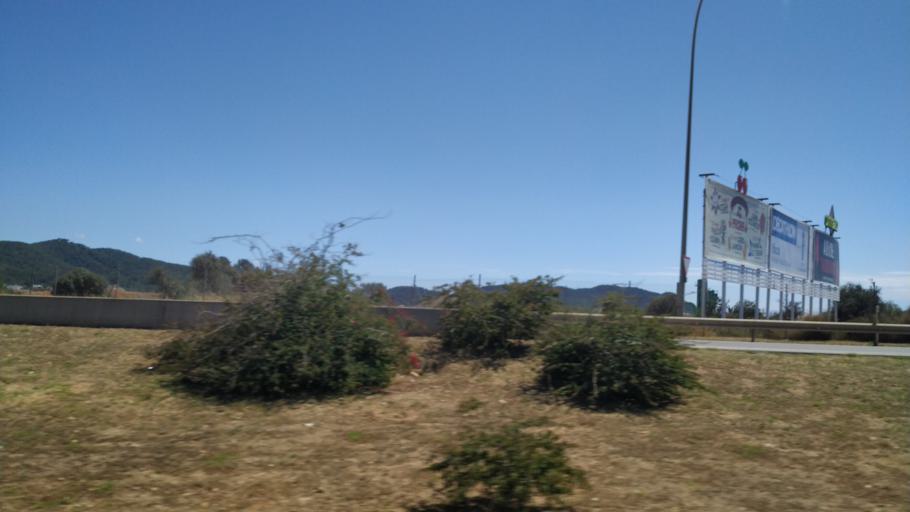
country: ES
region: Balearic Islands
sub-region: Illes Balears
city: Ibiza
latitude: 38.8822
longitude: 1.3818
